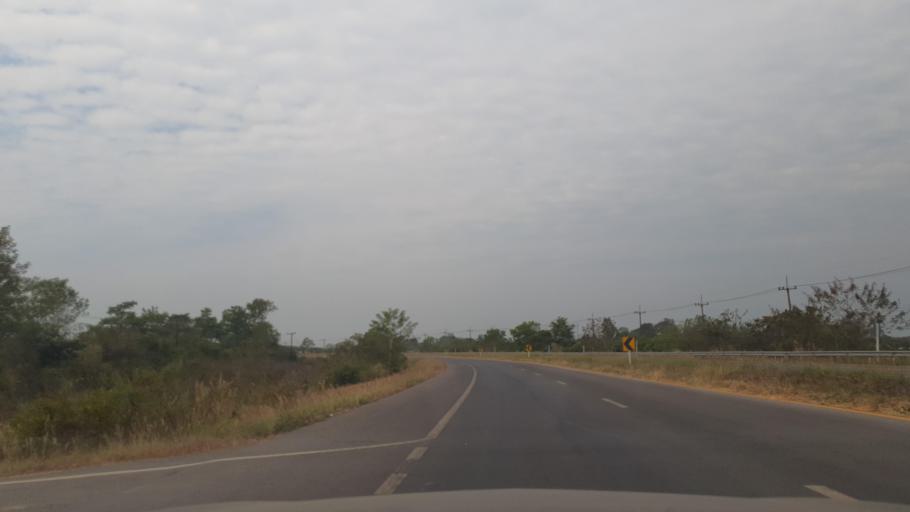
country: TH
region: Changwat Bueng Kan
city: Bung Khla
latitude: 18.3044
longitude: 103.9739
